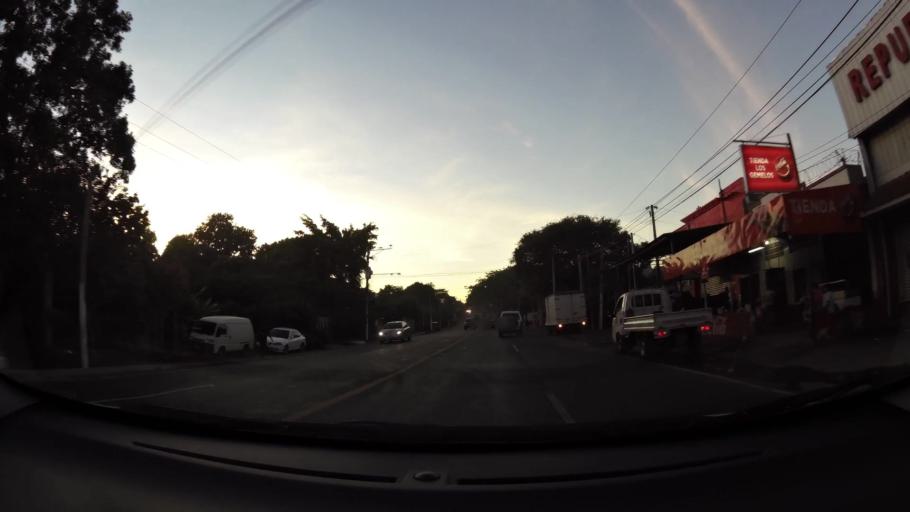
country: SV
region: San Miguel
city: San Miguel
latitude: 13.4983
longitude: -88.2073
